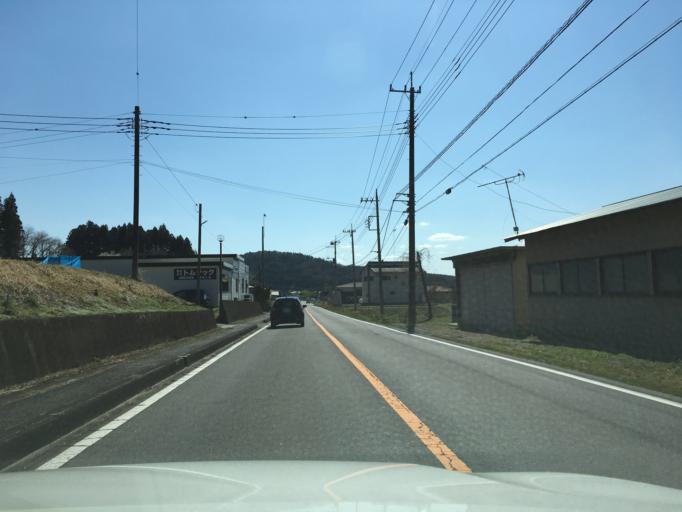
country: JP
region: Tochigi
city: Kuroiso
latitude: 36.9623
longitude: 140.1556
